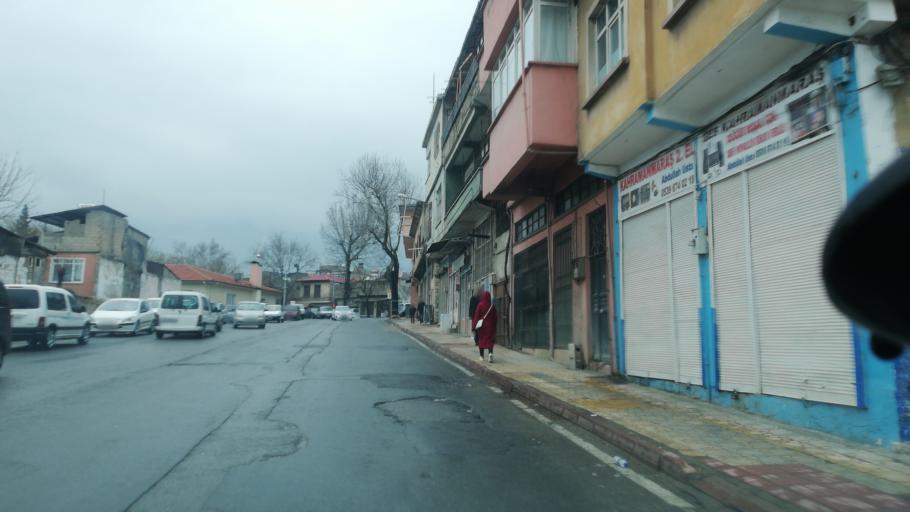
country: TR
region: Kahramanmaras
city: Kahramanmaras
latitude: 37.5837
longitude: 36.9306
